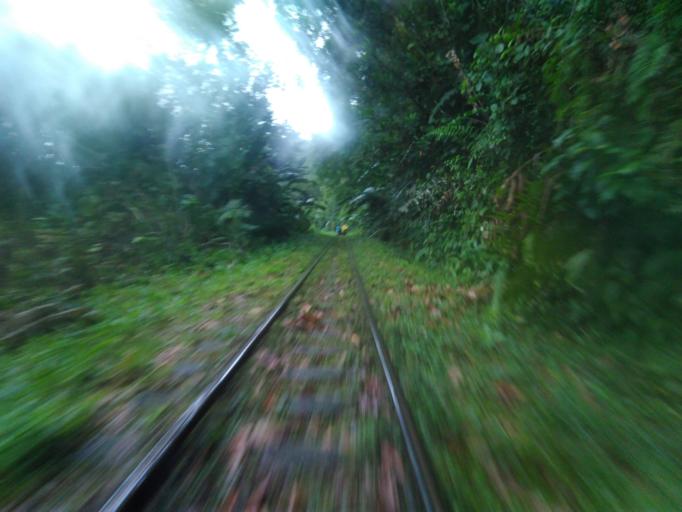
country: CO
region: Valle del Cauca
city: Buenaventura
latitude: 3.8464
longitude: -76.8645
